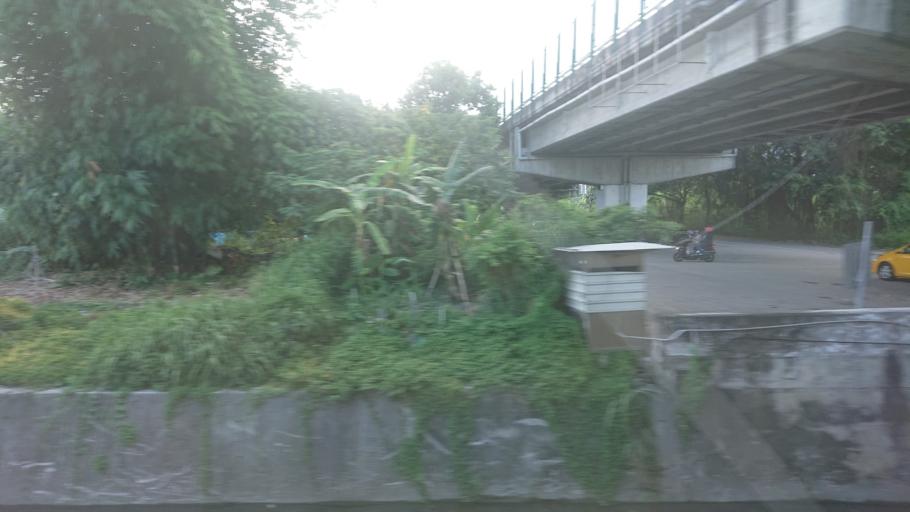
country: TW
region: Taiwan
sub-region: Hualien
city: Hualian
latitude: 23.9806
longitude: 121.5948
